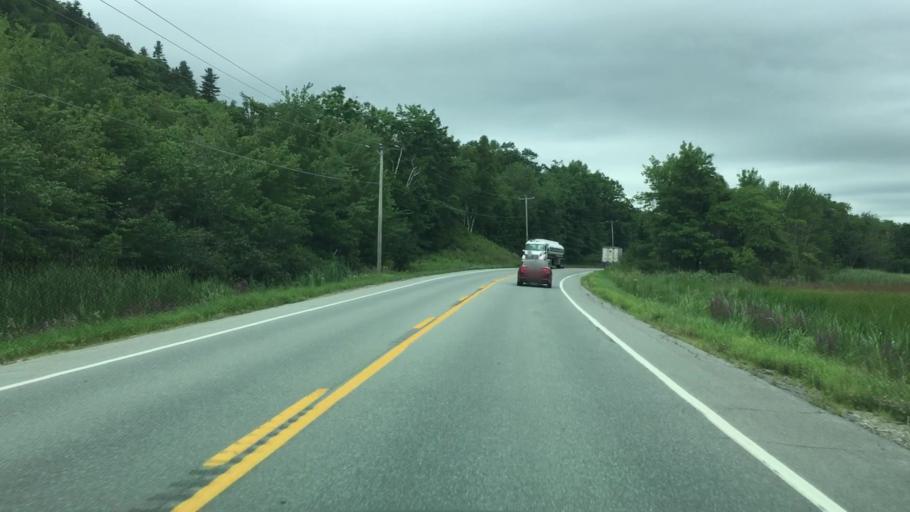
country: US
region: Maine
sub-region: Waldo County
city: Frankfort
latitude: 44.5797
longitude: -68.8624
